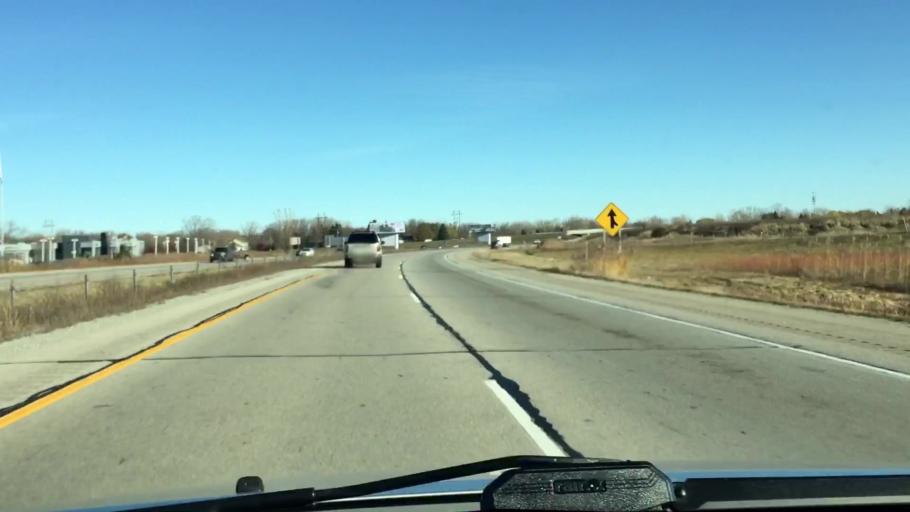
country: US
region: Wisconsin
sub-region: Outagamie County
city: Appleton
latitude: 44.2895
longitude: -88.4660
